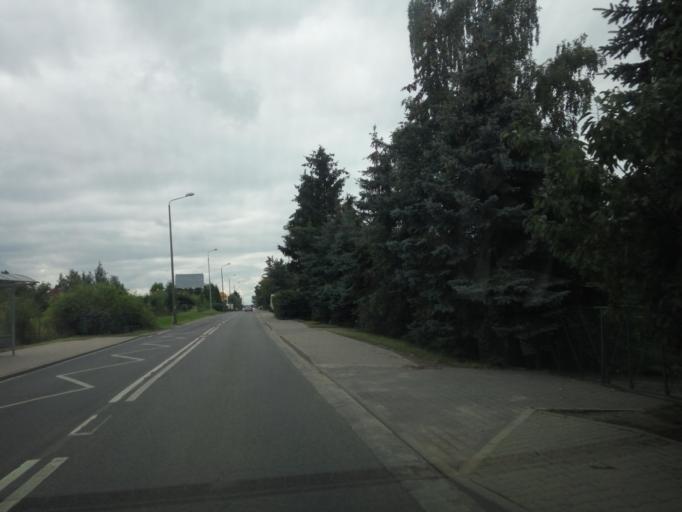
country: PL
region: Lower Silesian Voivodeship
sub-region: Powiat wroclawski
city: Zerniki Wroclawskie
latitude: 51.0543
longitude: 17.0320
